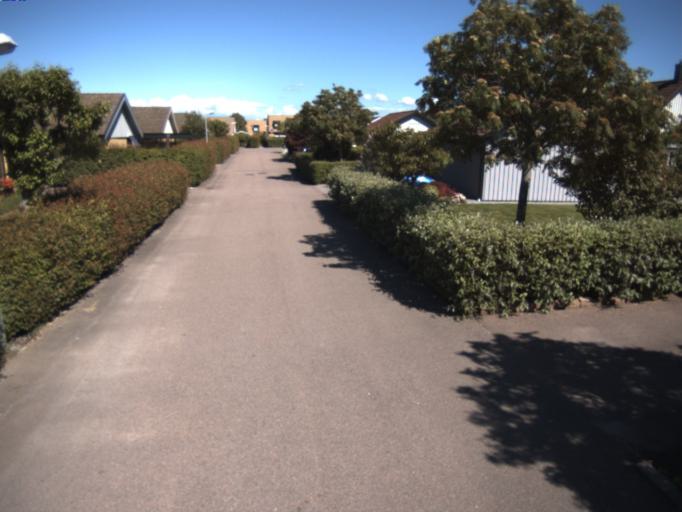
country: SE
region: Skane
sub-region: Helsingborg
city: Rydeback
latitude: 55.9598
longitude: 12.7690
